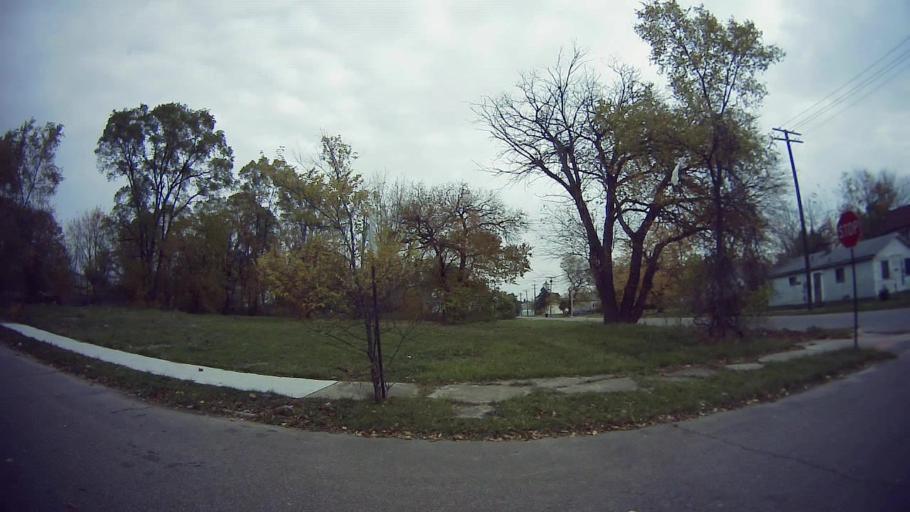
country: US
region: Michigan
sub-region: Wayne County
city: Hamtramck
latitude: 42.4064
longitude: -83.0675
